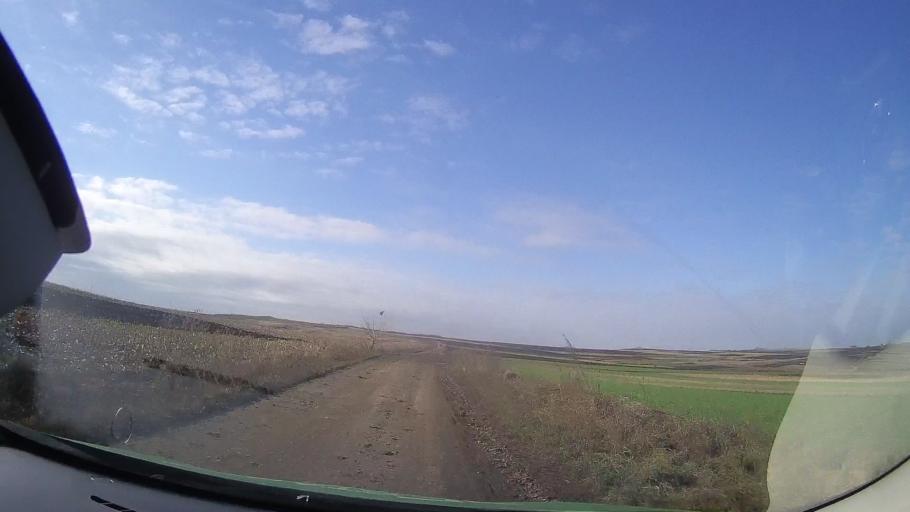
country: RO
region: Mures
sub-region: Comuna Saulia
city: Saulia
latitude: 46.5987
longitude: 24.2313
